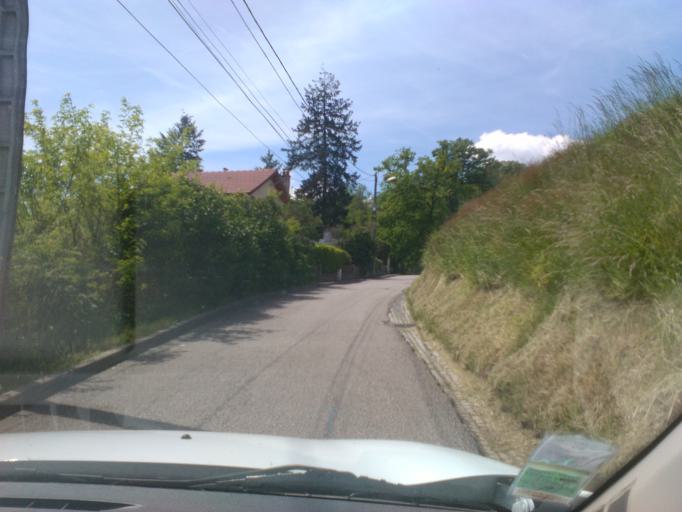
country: FR
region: Lorraine
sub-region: Departement des Vosges
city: Epinal
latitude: 48.1769
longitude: 6.4646
